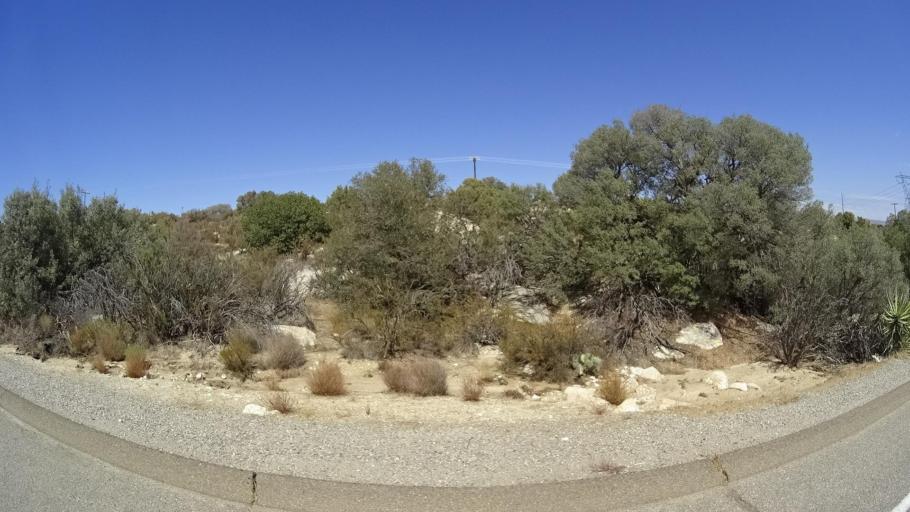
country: MX
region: Baja California
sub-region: Tecate
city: Cereso del Hongo
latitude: 32.6228
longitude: -116.2189
